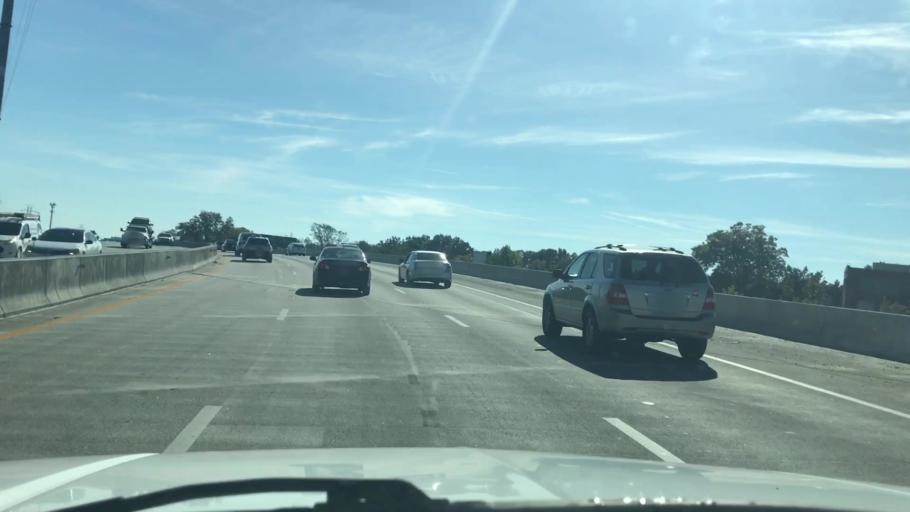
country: US
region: Virginia
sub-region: City of Richmond
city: Richmond
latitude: 37.5597
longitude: -77.4534
